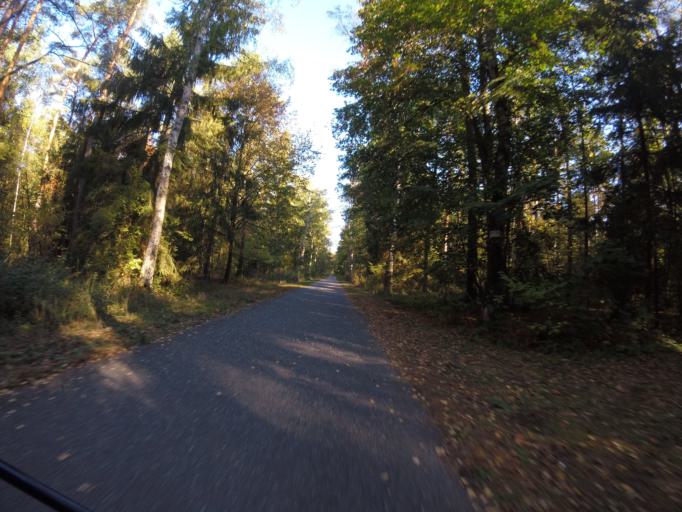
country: DE
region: Baden-Wuerttemberg
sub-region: Karlsruhe Region
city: Eggenstein-Leopoldshafen
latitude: 49.0521
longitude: 8.4084
